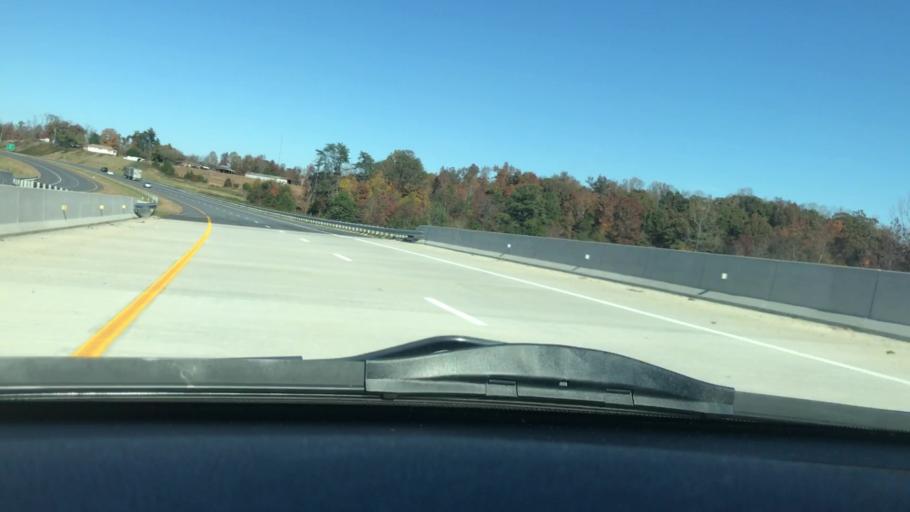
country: US
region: North Carolina
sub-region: Guilford County
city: Summerfield
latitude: 36.1777
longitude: -79.9340
